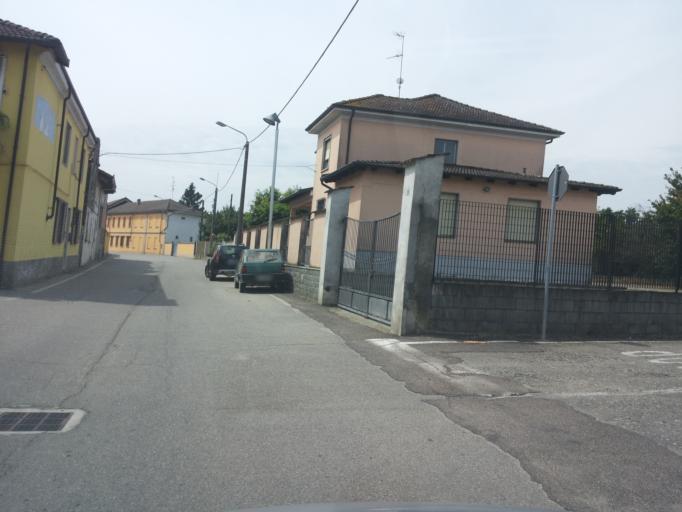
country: IT
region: Piedmont
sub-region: Provincia di Vercelli
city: Pezzana
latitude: 45.2601
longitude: 8.4823
